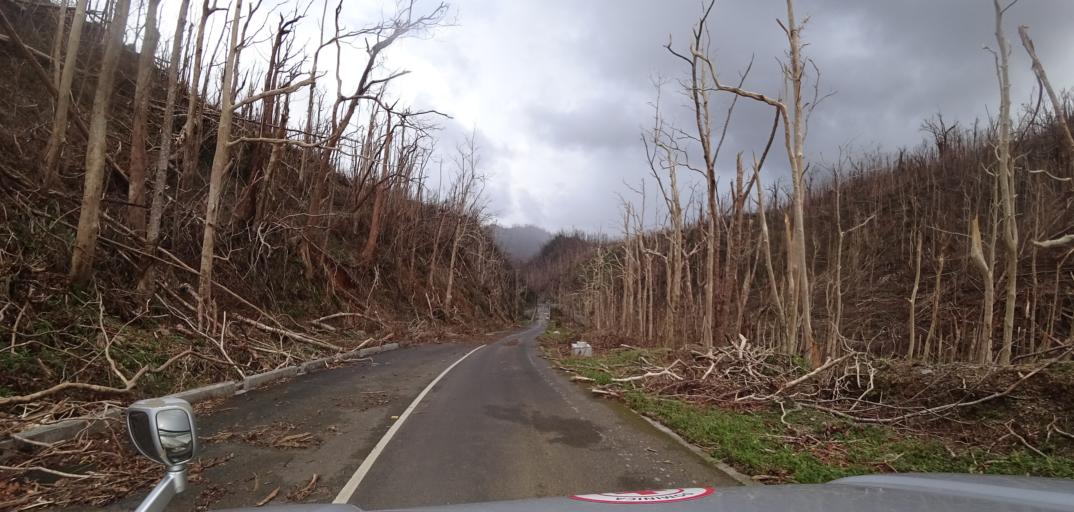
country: DM
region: Saint David
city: Castle Bruce
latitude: 15.4671
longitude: -61.3033
